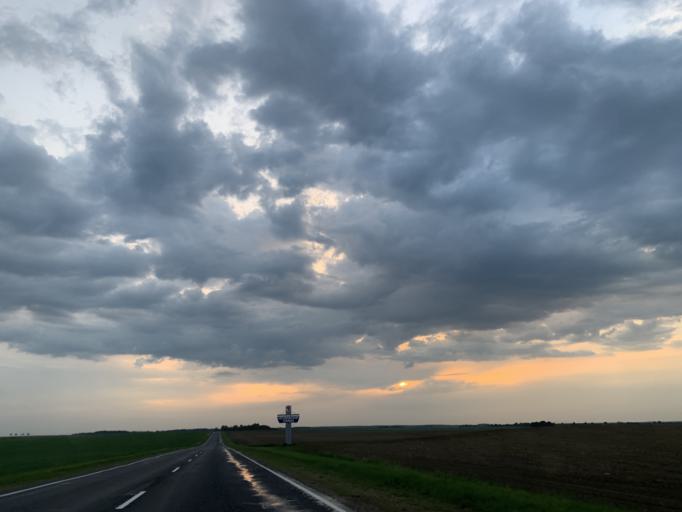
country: BY
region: Minsk
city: Nyasvizh
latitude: 53.1485
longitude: 26.8272
